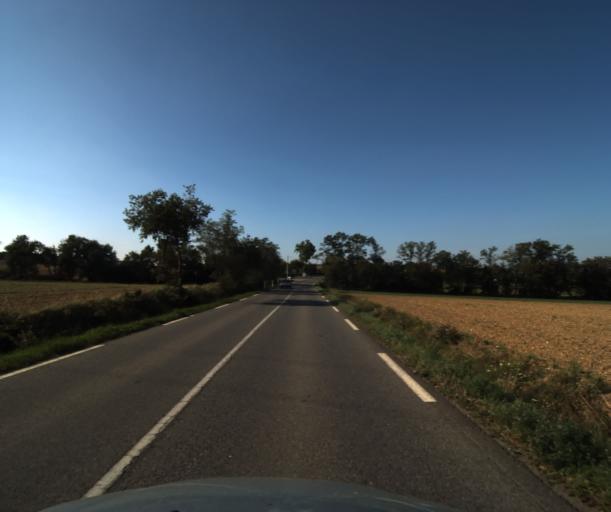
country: FR
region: Midi-Pyrenees
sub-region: Departement de la Haute-Garonne
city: Labarthe-sur-Leze
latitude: 43.4358
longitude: 1.3786
